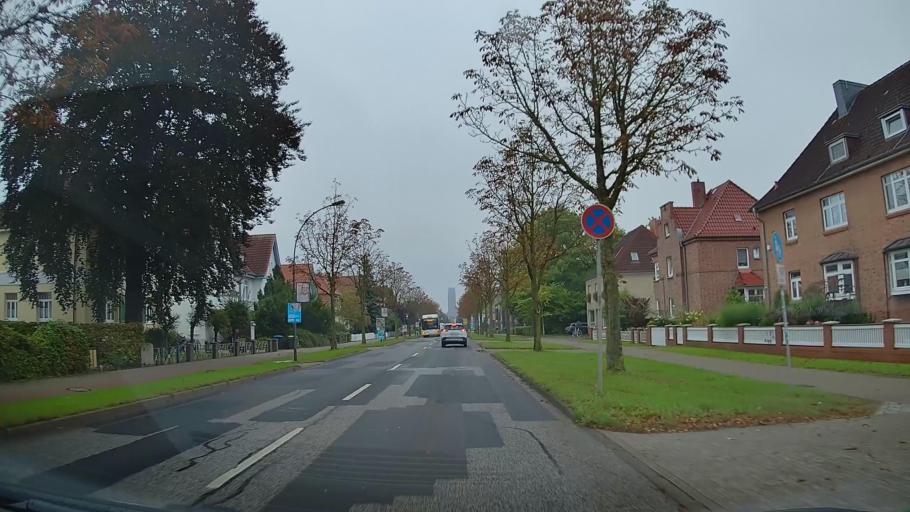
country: DE
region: Mecklenburg-Vorpommern
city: Wismar
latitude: 53.8941
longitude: 11.4429
